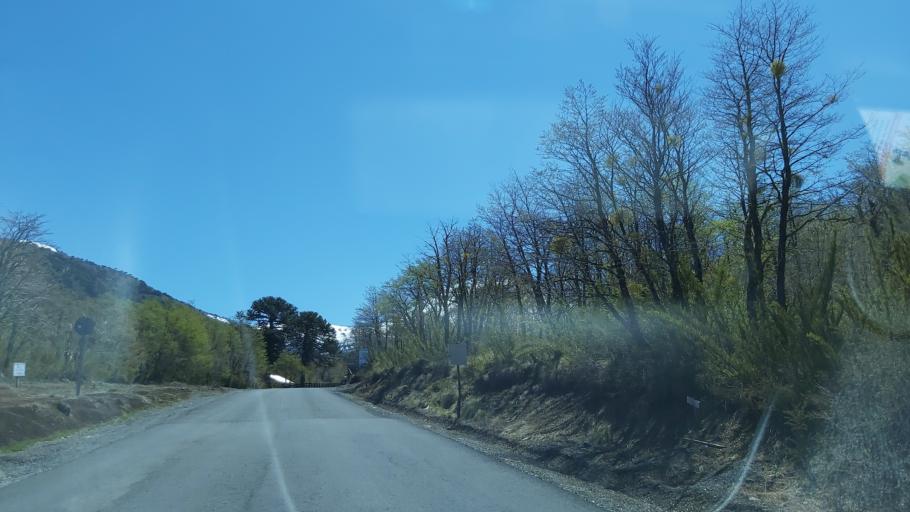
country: CL
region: Araucania
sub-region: Provincia de Cautin
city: Vilcun
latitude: -38.4408
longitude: -71.5262
